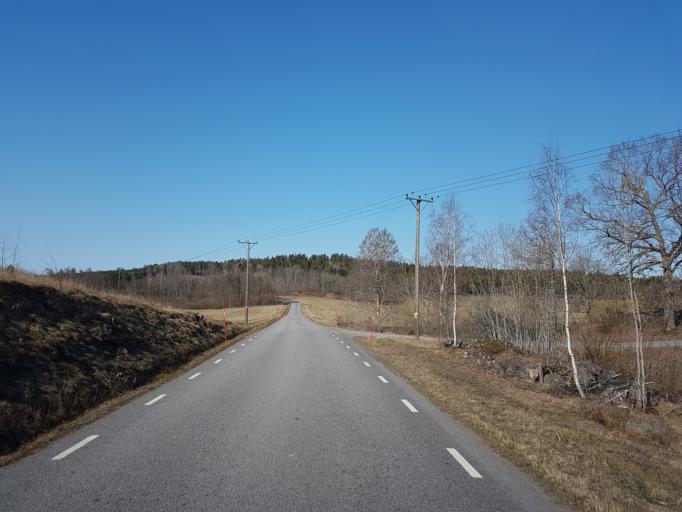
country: SE
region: OEstergoetland
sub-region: Valdemarsviks Kommun
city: Gusum
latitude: 58.2005
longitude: 16.3516
